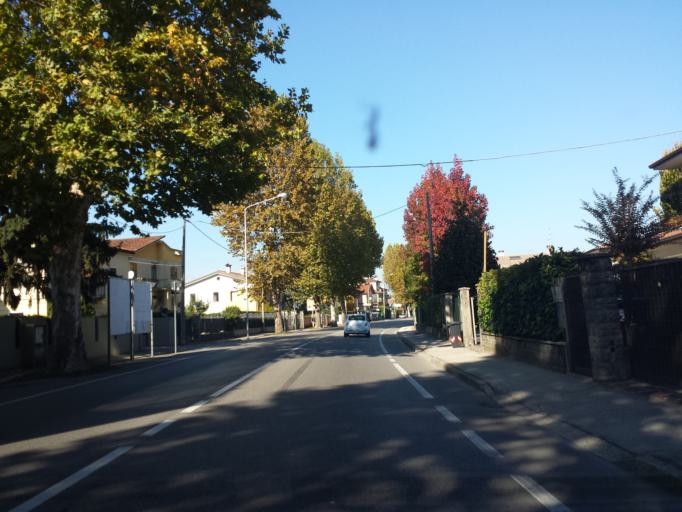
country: IT
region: Veneto
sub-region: Provincia di Vicenza
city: Crispi Cavour
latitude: 45.5648
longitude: 11.5160
